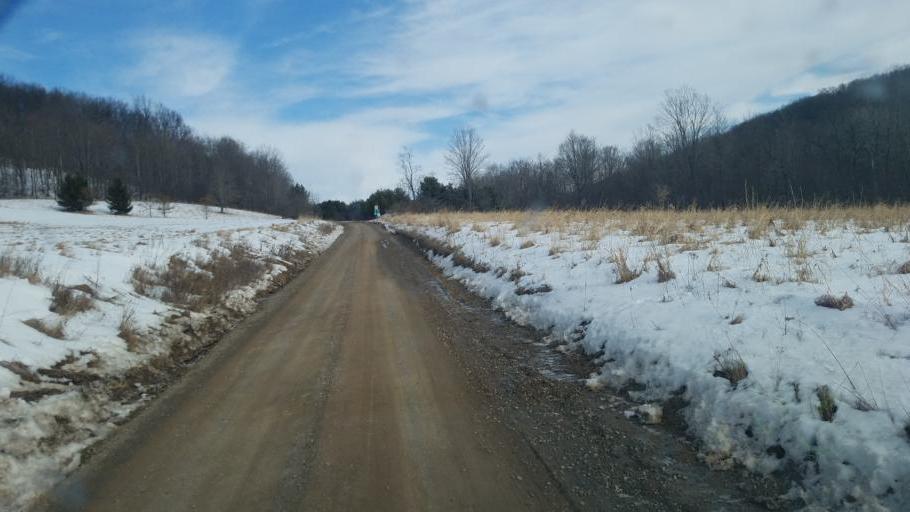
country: US
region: New York
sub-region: Allegany County
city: Andover
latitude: 41.9971
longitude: -77.8178
